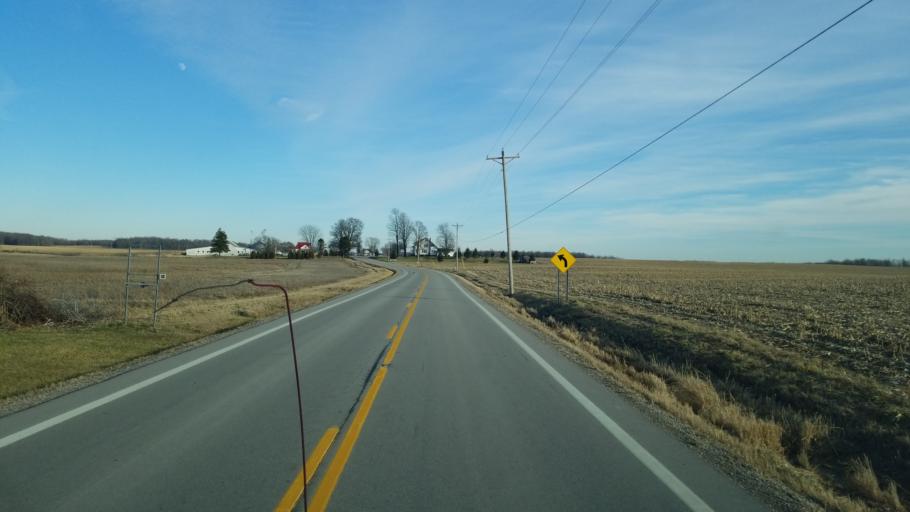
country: US
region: Ohio
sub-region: Huron County
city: Greenwich
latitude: 41.1033
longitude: -82.5531
